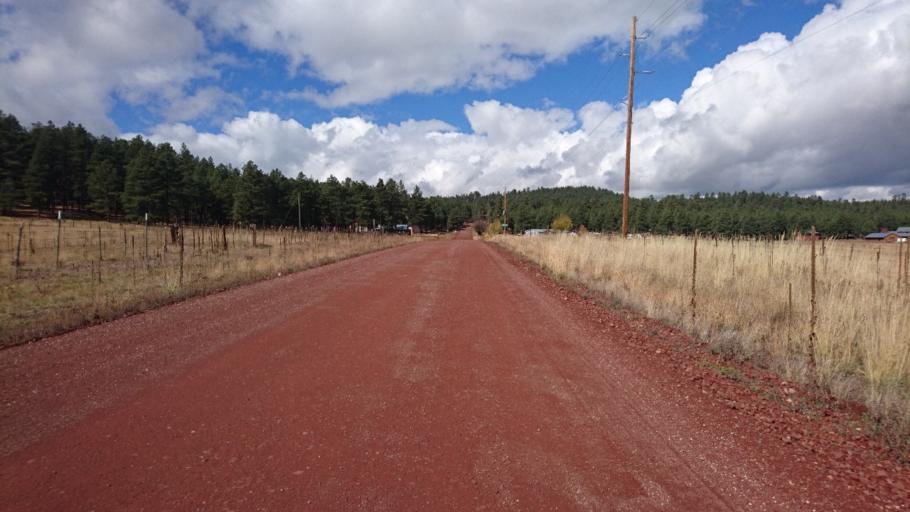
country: US
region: Arizona
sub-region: Coconino County
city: Parks
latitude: 35.2718
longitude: -111.8912
